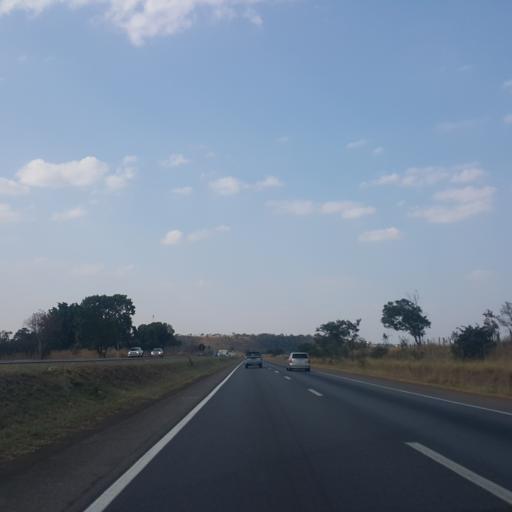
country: BR
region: Goias
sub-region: Abadiania
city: Abadiania
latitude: -16.1108
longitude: -48.5287
